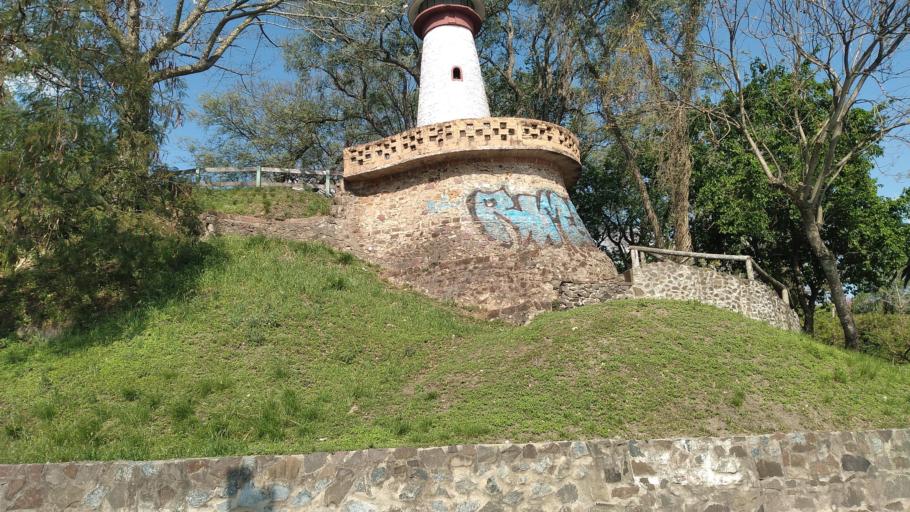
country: AR
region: Entre Rios
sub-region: Departamento de La Paz
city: La Paz
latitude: -30.7374
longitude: -59.6468
